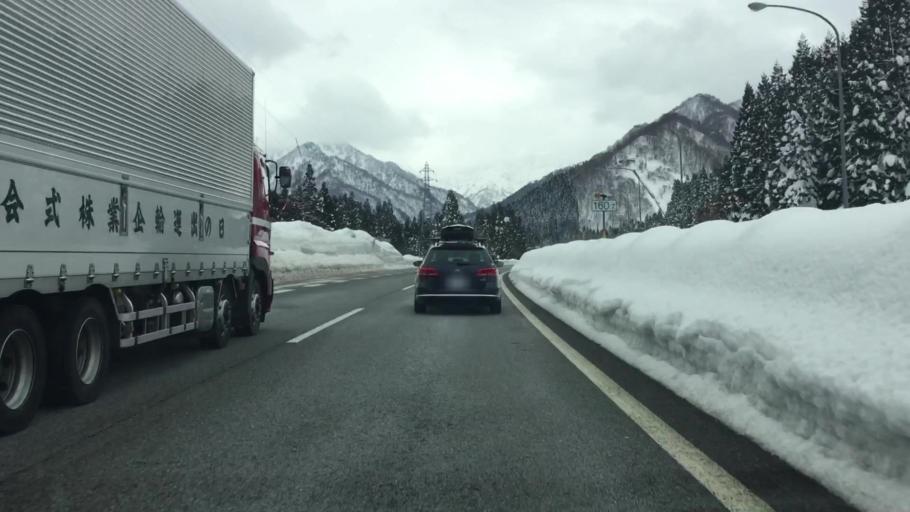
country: JP
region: Niigata
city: Shiozawa
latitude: 36.8855
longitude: 138.8509
